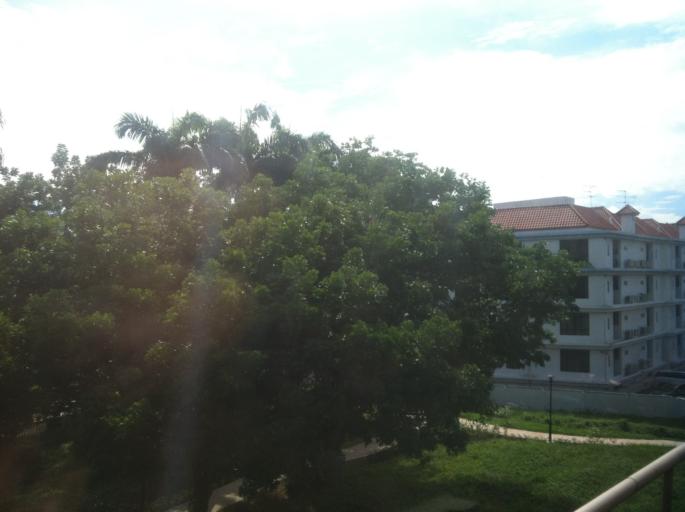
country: SG
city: Singapore
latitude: 1.3201
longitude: 103.9059
